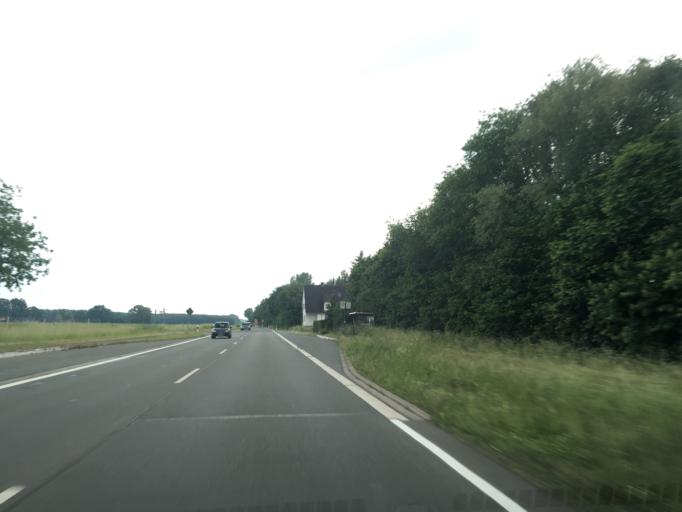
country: DE
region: North Rhine-Westphalia
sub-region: Regierungsbezirk Munster
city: Muenster
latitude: 52.0272
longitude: 7.6185
